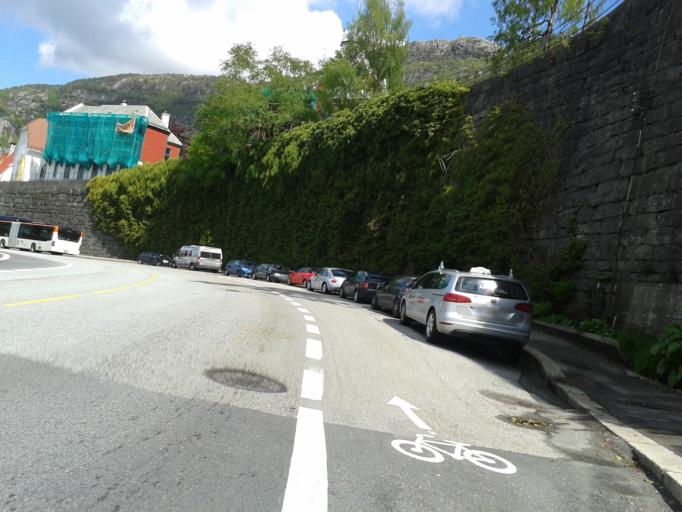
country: NO
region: Hordaland
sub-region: Bergen
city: Bergen
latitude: 60.4054
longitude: 5.3236
